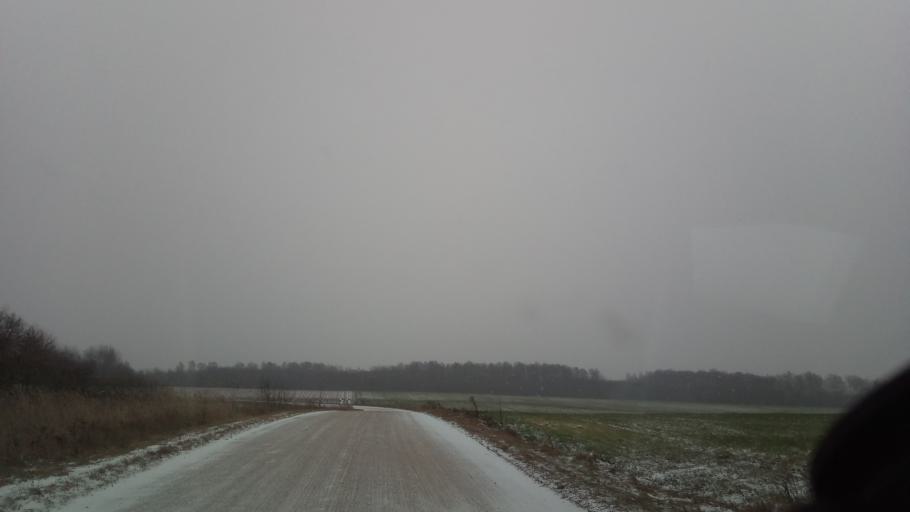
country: LT
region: Vilnius County
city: Ukmerge
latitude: 55.3213
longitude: 24.9634
